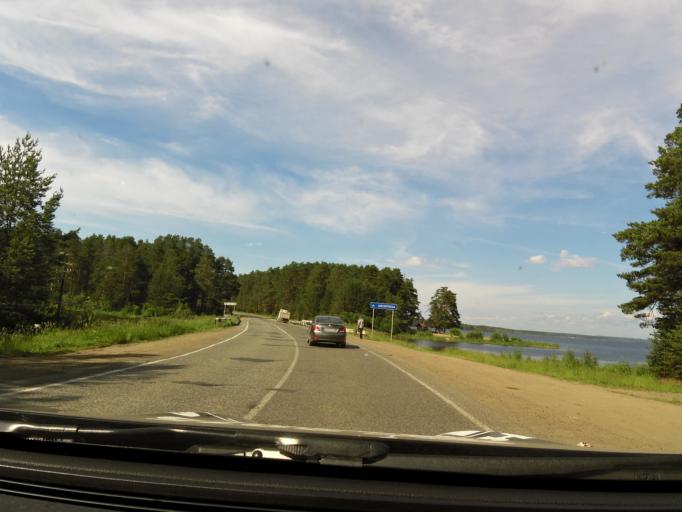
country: RU
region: Kirov
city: Belaya Kholunitsa
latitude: 58.8592
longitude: 50.8420
